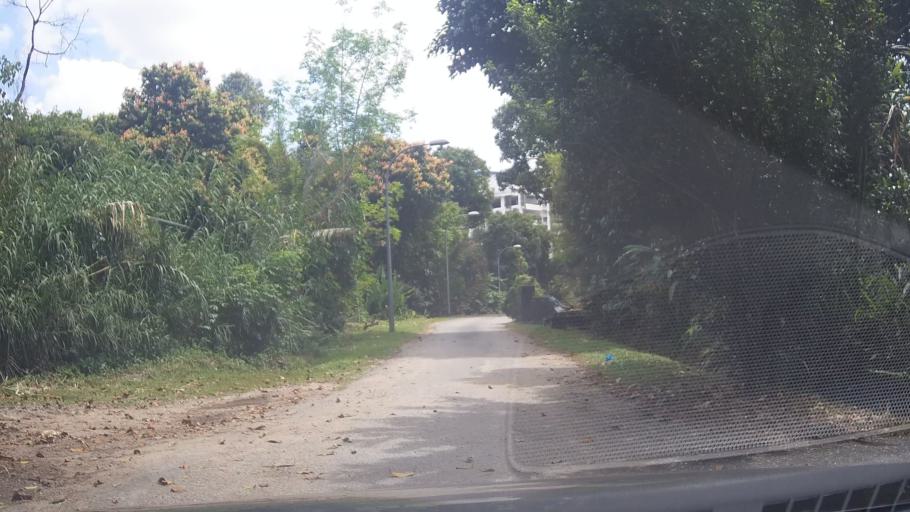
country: MY
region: Johor
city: Johor Bahru
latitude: 1.4533
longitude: 103.7889
